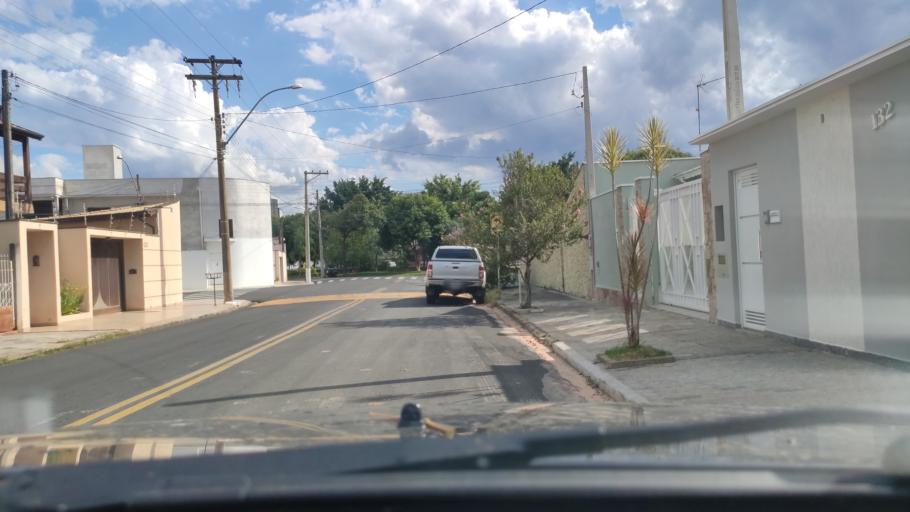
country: BR
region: Sao Paulo
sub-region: Itapira
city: Itapira
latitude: -22.4269
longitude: -46.8261
